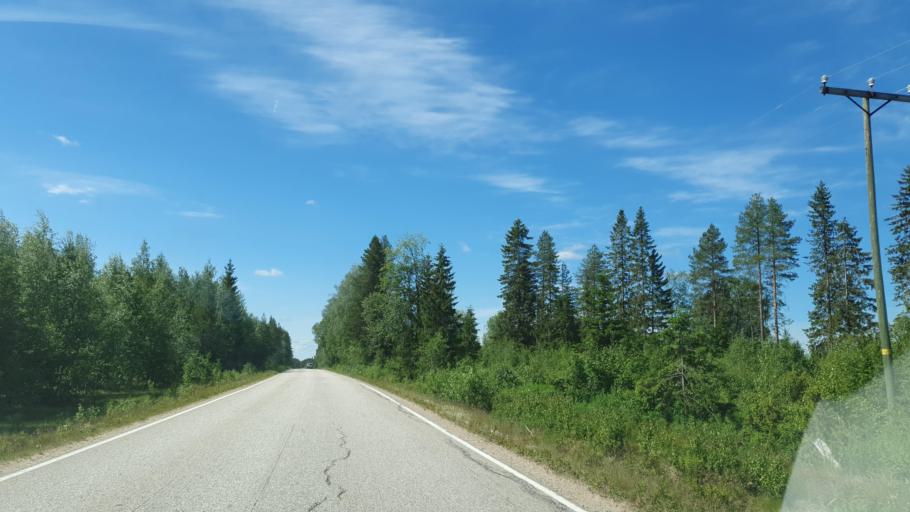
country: FI
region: Kainuu
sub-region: Kehys-Kainuu
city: Suomussalmi
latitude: 64.5876
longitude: 29.0667
